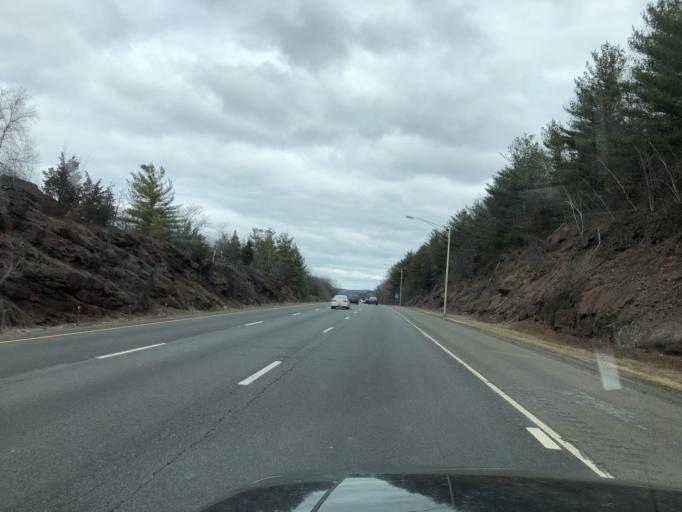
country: US
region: Connecticut
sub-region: Hartford County
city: Plainville
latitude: 41.6367
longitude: -72.8679
